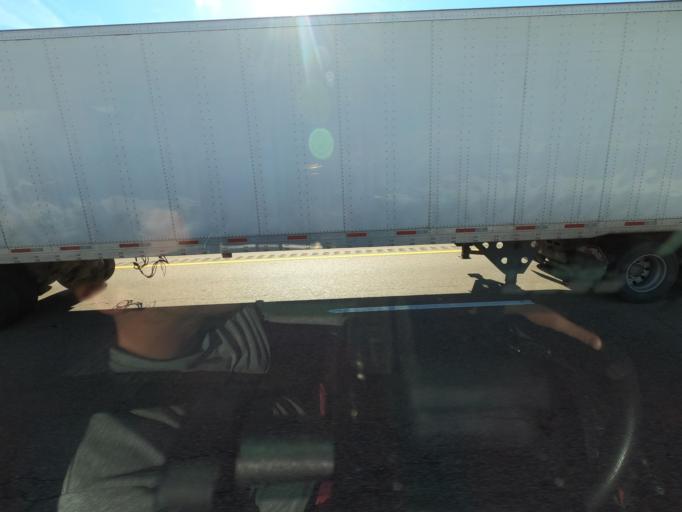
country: US
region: Tennessee
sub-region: Shelby County
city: Bartlett
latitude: 35.1576
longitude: -89.8933
